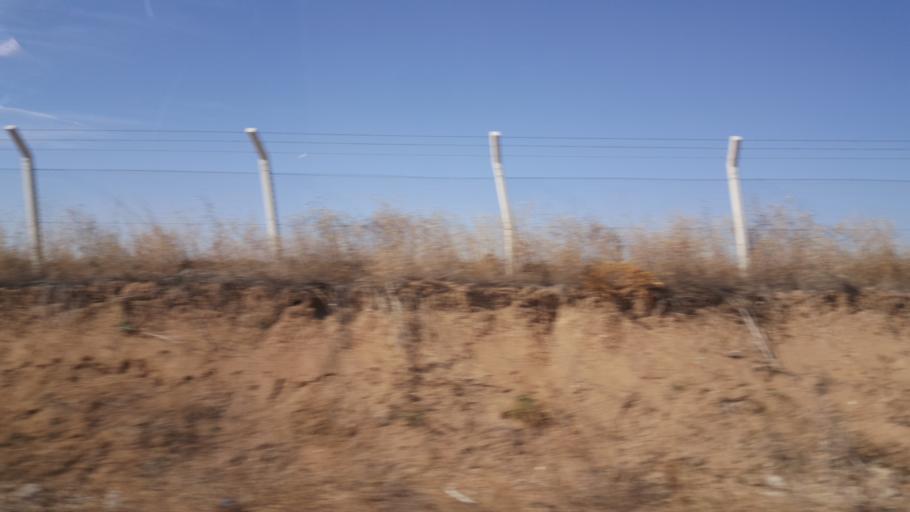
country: TR
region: Ankara
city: Ikizce
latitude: 39.6116
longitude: 32.6821
